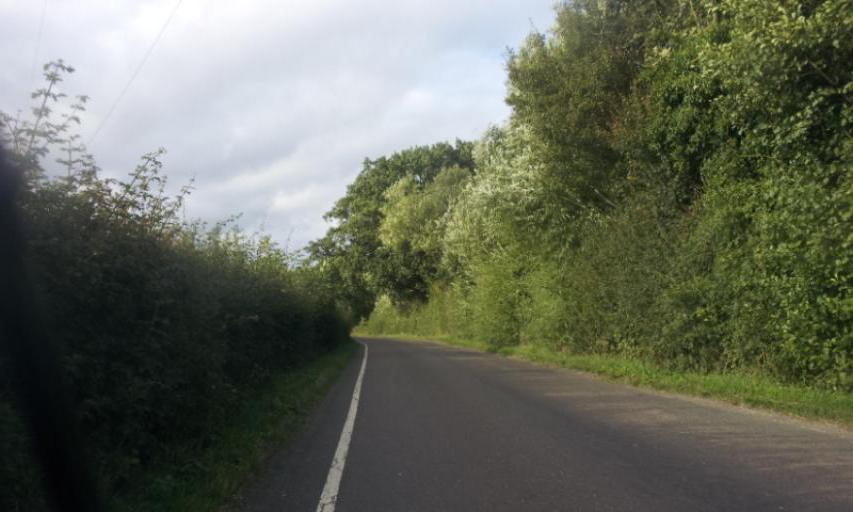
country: GB
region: England
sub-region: Kent
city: Hadlow
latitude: 51.1991
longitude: 0.3309
